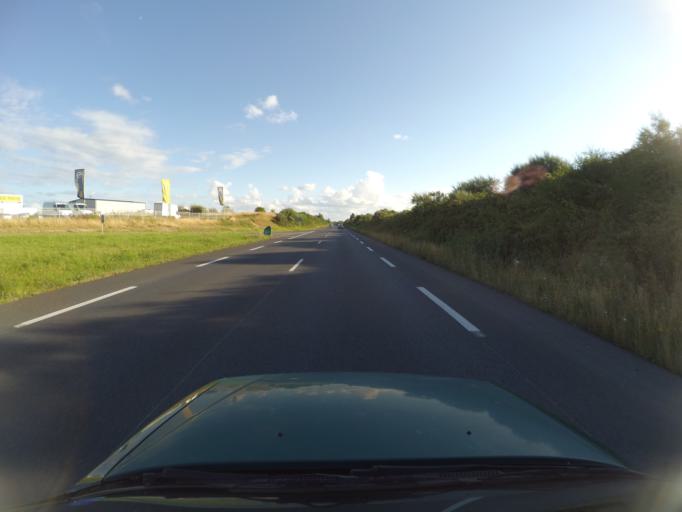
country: FR
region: Pays de la Loire
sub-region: Departement de la Vendee
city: Saint-Hilaire-de-Loulay
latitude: 47.0040
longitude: -1.3432
